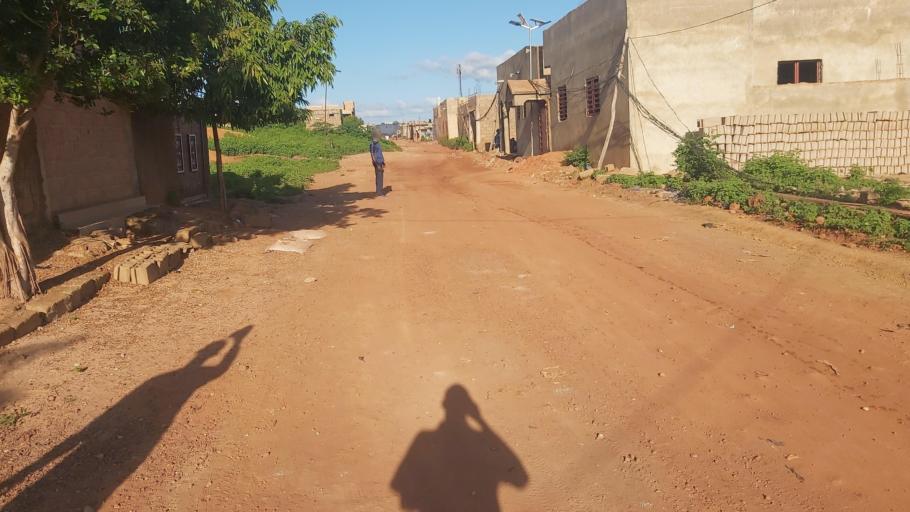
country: ML
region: Bamako
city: Bamako
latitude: 12.6265
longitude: -7.9047
